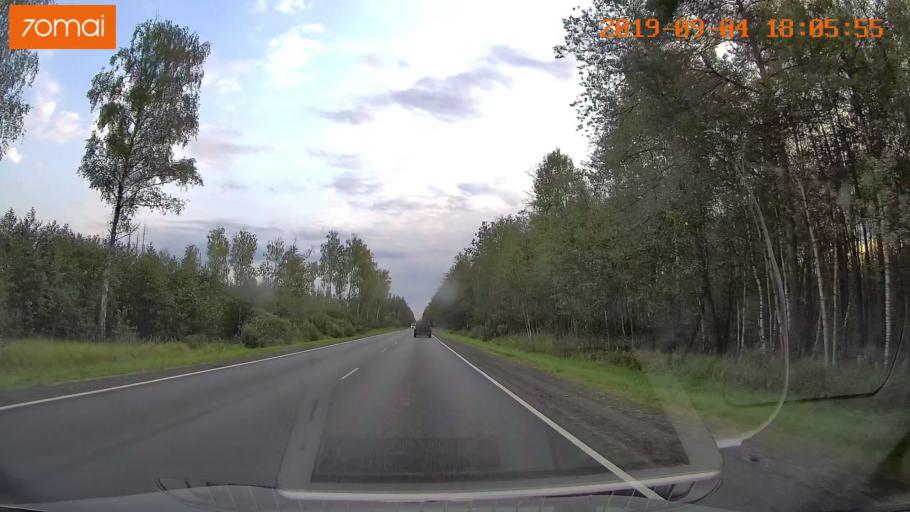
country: RU
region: Moskovskaya
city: Il'inskiy Pogost
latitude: 55.4362
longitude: 38.8207
